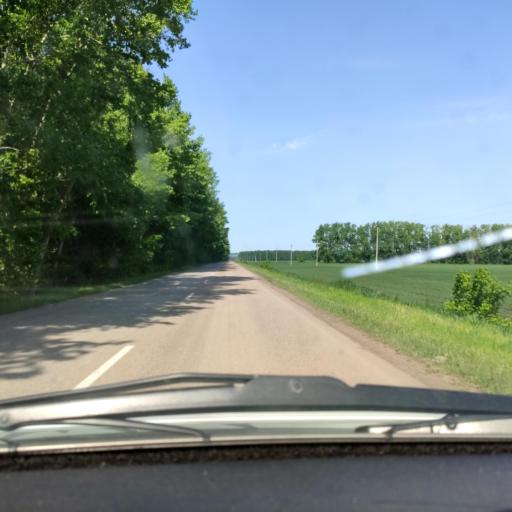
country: RU
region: Bashkortostan
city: Avdon
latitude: 54.5100
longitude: 55.6242
